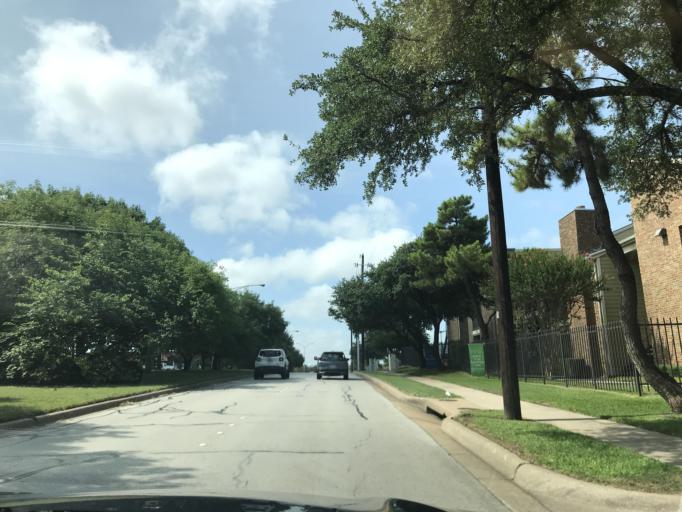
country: US
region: Texas
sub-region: Tarrant County
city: Benbrook
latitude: 32.6784
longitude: -97.4033
